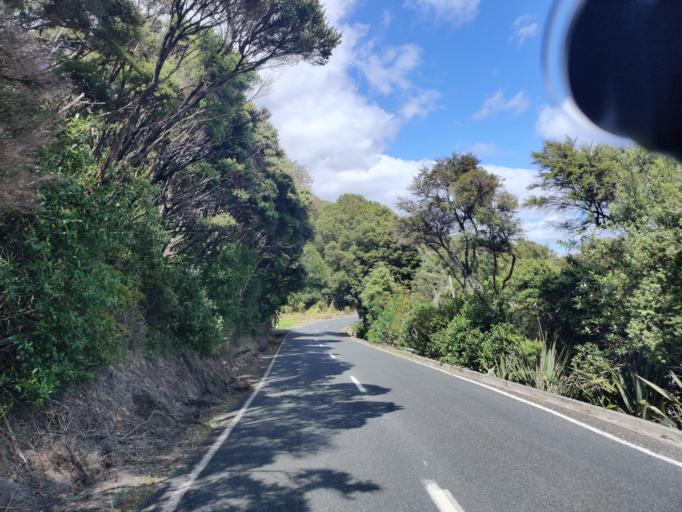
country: NZ
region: Northland
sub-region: Far North District
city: Paihia
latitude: -35.2566
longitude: 174.2369
